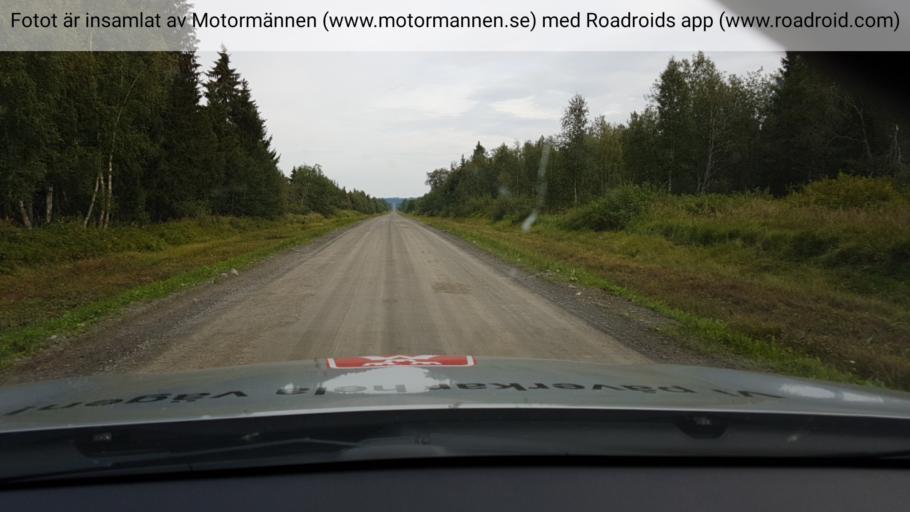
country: SE
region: Jaemtland
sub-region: OEstersunds Kommun
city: Lit
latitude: 63.6796
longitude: 14.8619
